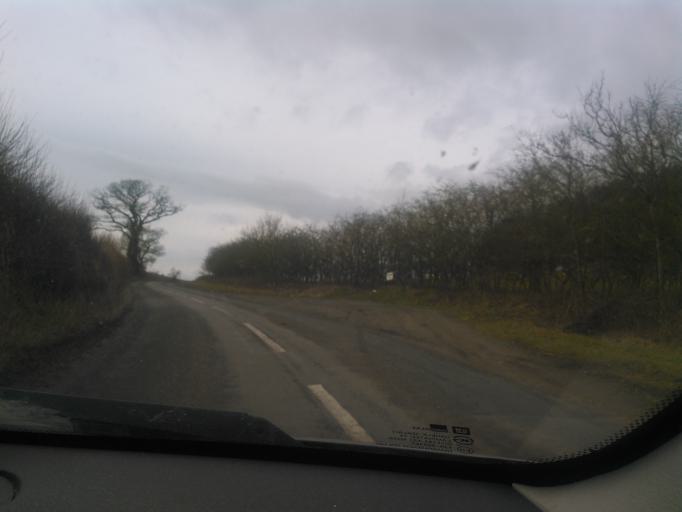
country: GB
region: England
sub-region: Shropshire
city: Clive
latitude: 52.8225
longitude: -2.6784
